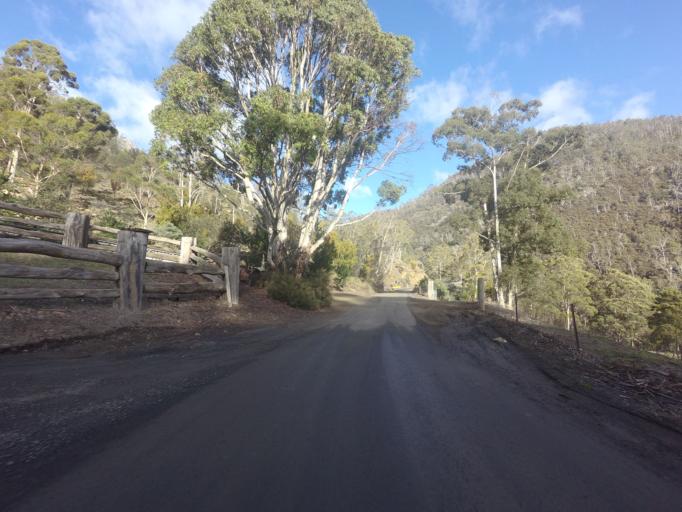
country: AU
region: Tasmania
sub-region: Glenorchy
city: Berriedale
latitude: -42.8176
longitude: 147.1793
